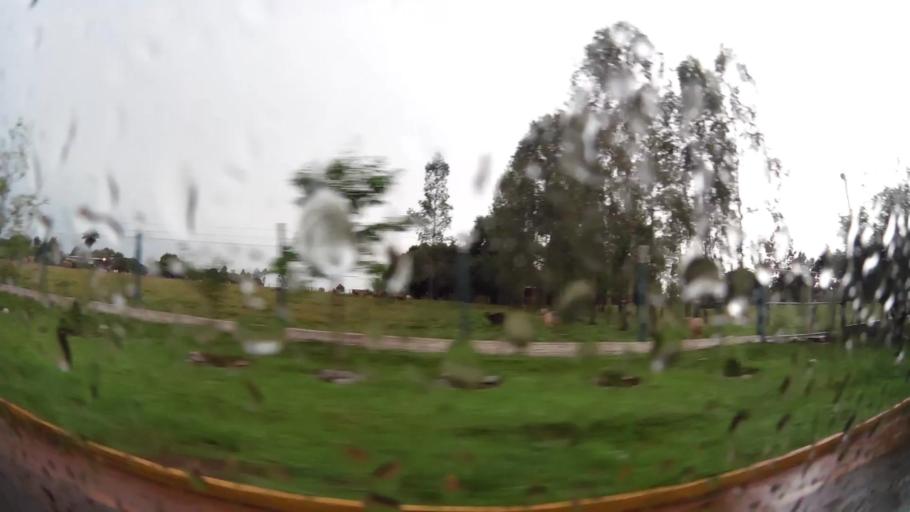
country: PY
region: Alto Parana
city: Presidente Franco
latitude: -25.5334
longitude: -54.6787
